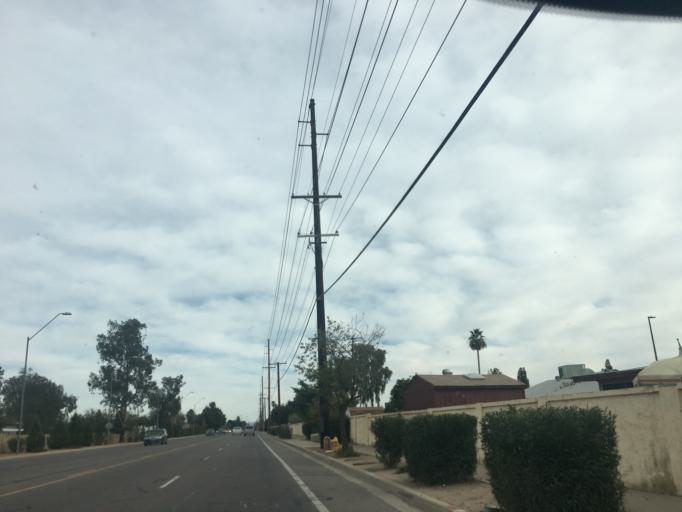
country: US
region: Arizona
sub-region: Maricopa County
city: Gilbert
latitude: 33.3643
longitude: -111.7977
